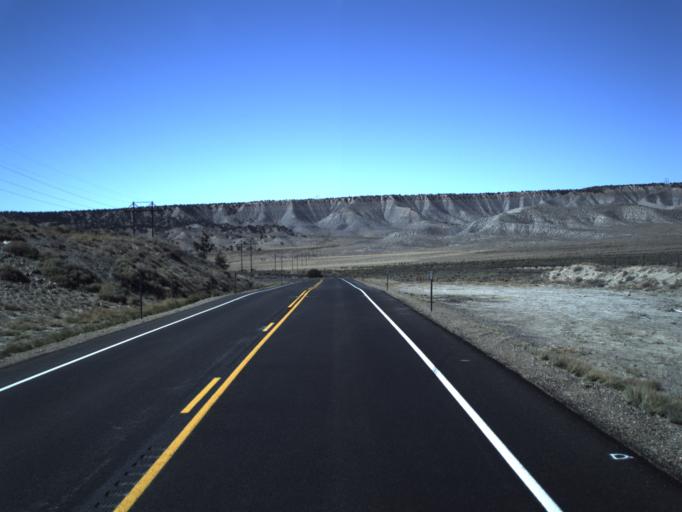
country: US
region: Utah
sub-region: Garfield County
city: Panguitch
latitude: 37.6019
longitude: -111.9599
